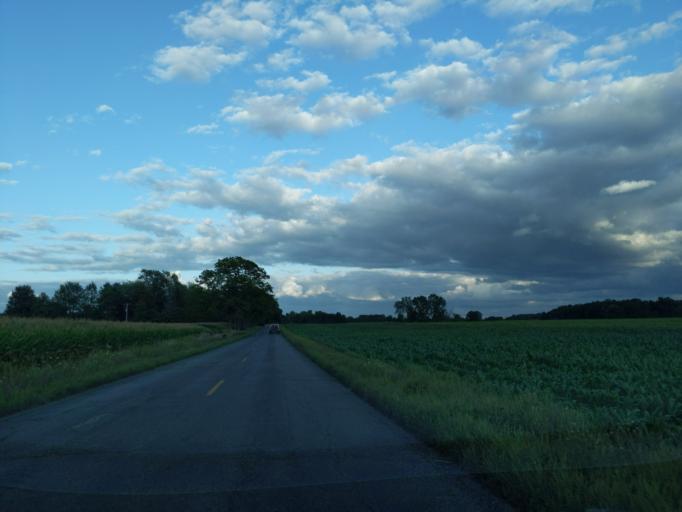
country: US
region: Michigan
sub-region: Ingham County
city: Holt
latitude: 42.5968
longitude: -84.5605
